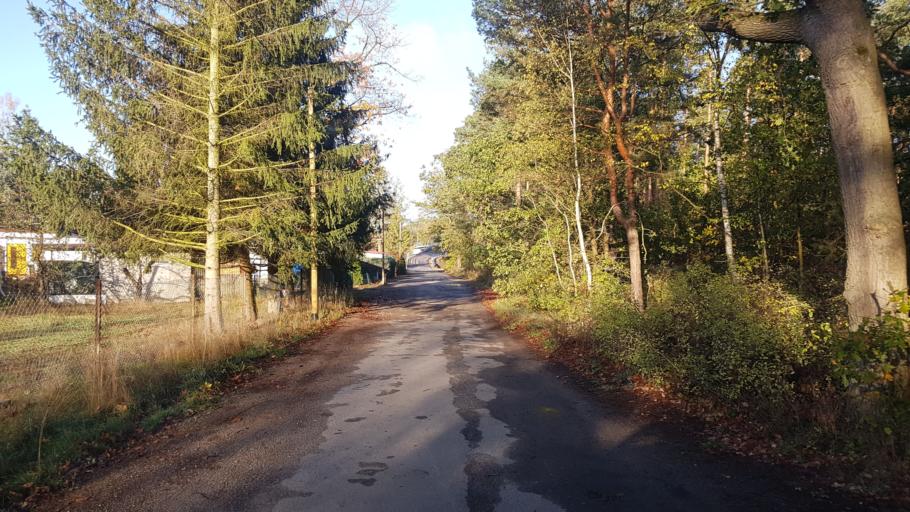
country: DE
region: Brandenburg
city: Ruckersdorf
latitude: 51.5931
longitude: 13.5726
